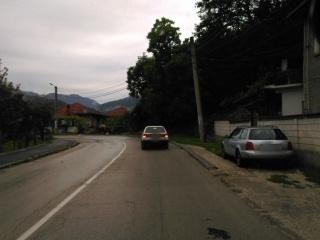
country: BG
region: Lovech
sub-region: Obshtina Troyan
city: Troyan
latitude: 42.8662
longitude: 24.7066
